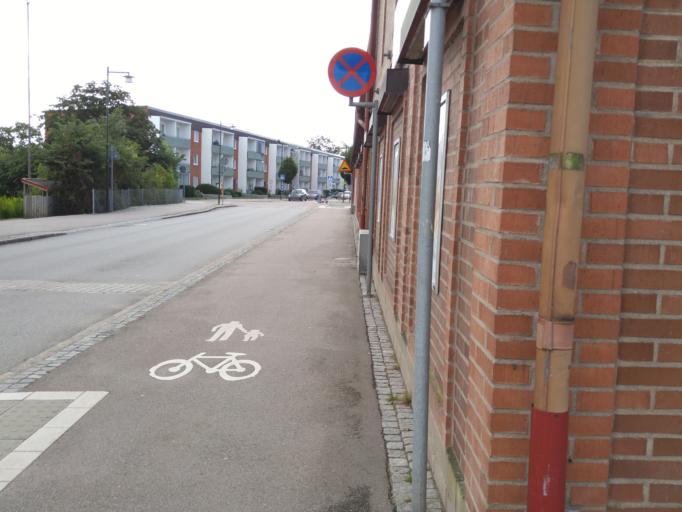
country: SE
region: Skane
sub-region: Hoors Kommun
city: Hoeoer
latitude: 55.9345
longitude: 13.5396
